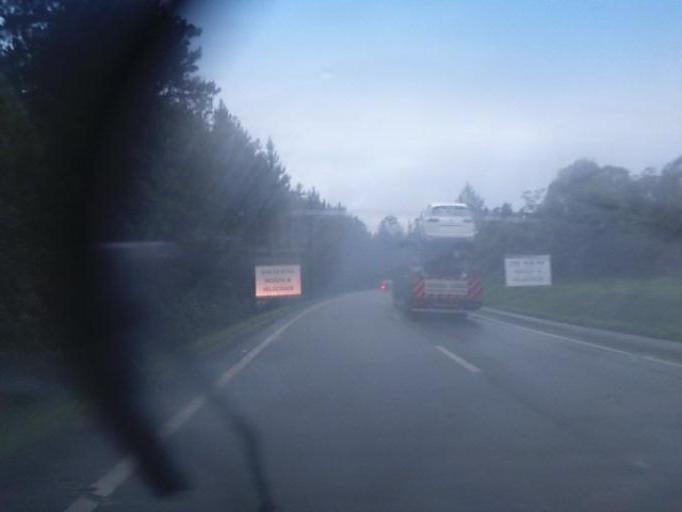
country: BR
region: Parana
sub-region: Sao Jose Dos Pinhais
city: Sao Jose dos Pinhais
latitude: -25.8518
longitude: -49.0310
